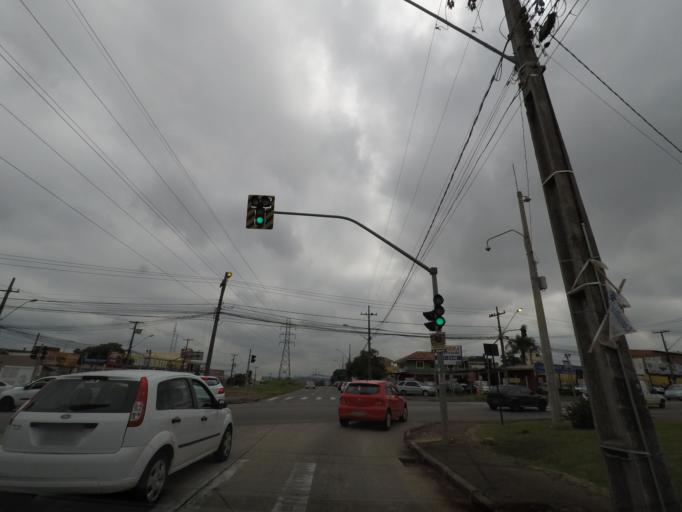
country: BR
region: Parana
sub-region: Curitiba
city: Curitiba
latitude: -25.5037
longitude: -49.3146
